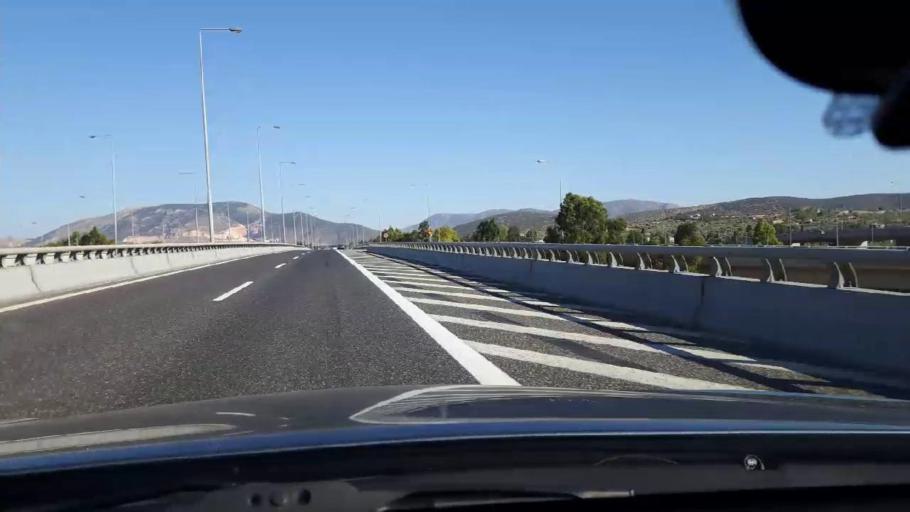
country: GR
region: Attica
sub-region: Nomarchia Anatolikis Attikis
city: Markopoulo
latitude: 37.8985
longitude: 23.9073
